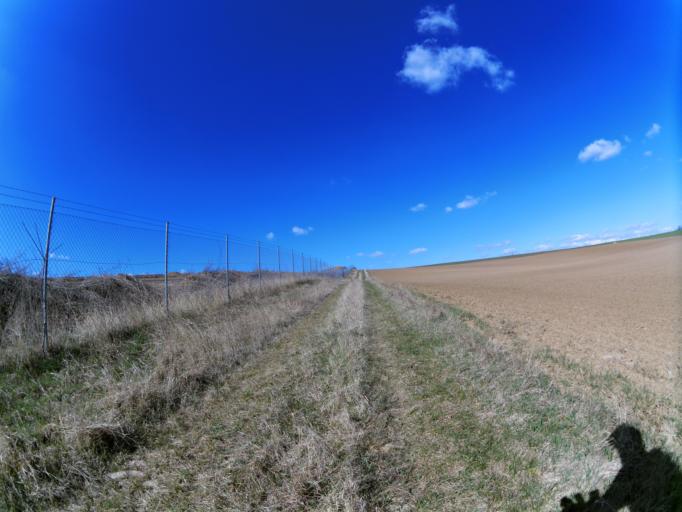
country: DE
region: Bavaria
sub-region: Regierungsbezirk Unterfranken
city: Greussenheim
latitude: 49.8017
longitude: 9.7774
